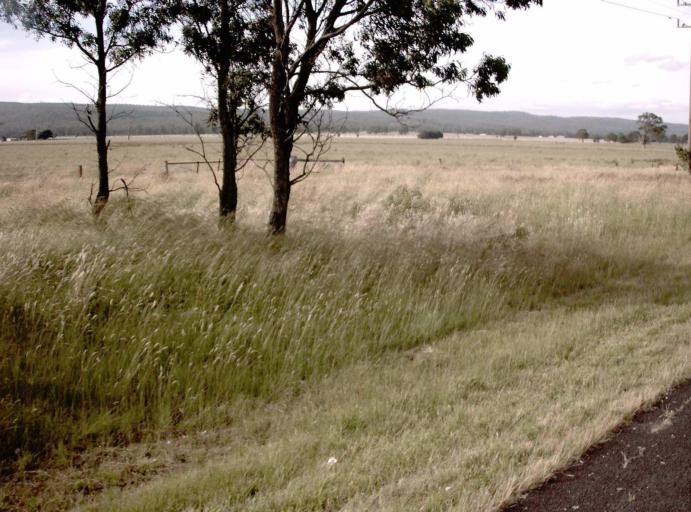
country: AU
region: Victoria
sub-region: Latrobe
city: Traralgon
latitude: -38.0899
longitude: 146.6018
